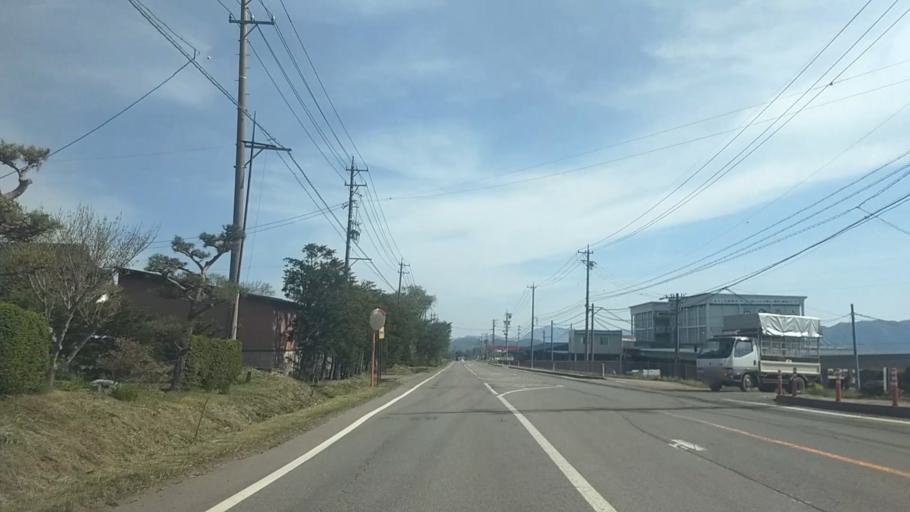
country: JP
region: Nagano
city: Saku
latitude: 35.9811
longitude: 138.4841
